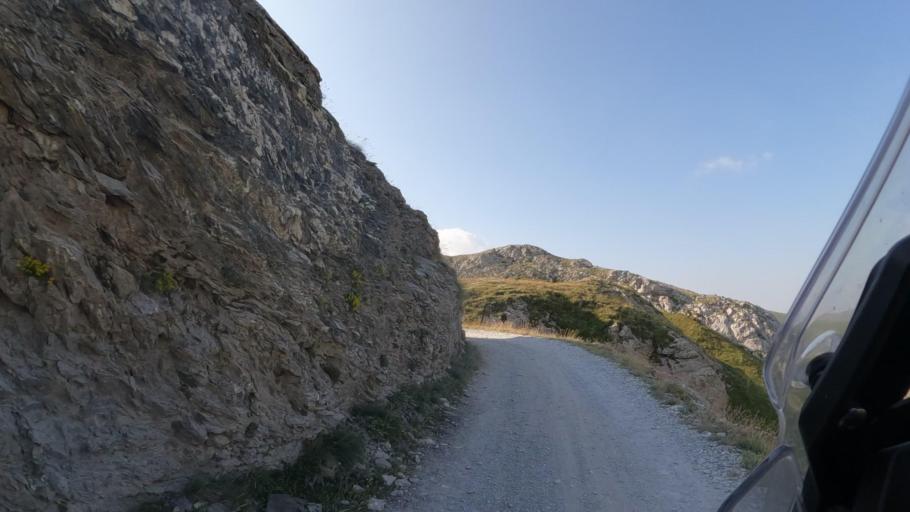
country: IT
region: Piedmont
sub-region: Provincia di Cuneo
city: Limone Piemonte
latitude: 44.1706
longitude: 7.6394
